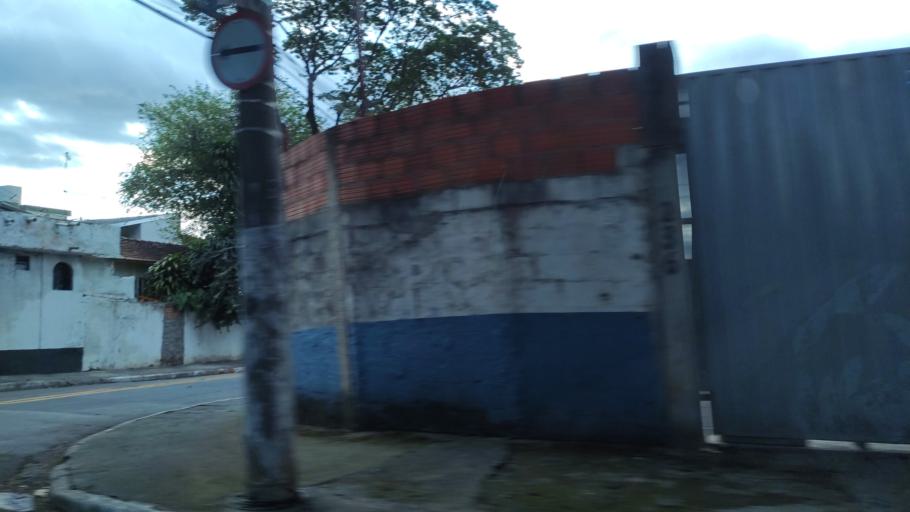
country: BR
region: Sao Paulo
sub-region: Sao Jose Dos Campos
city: Sao Jose dos Campos
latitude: -23.2307
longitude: -45.9030
